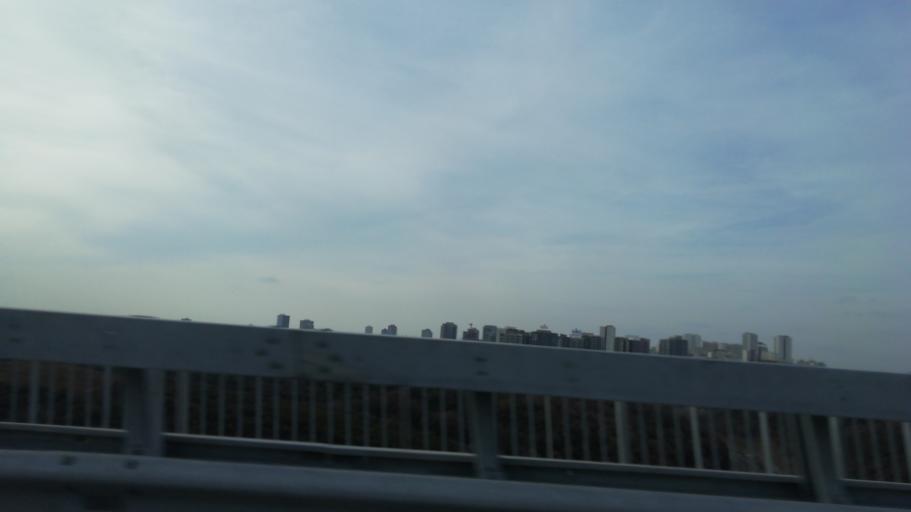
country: TR
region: Istanbul
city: Basaksehir
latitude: 41.1238
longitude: 28.7981
